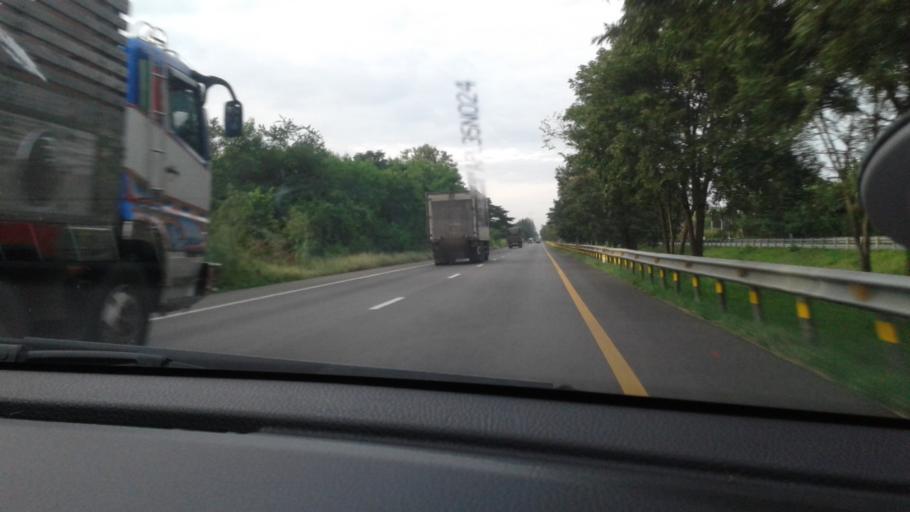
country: TH
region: Prachuap Khiri Khan
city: Pran Buri
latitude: 12.4677
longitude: 99.8961
